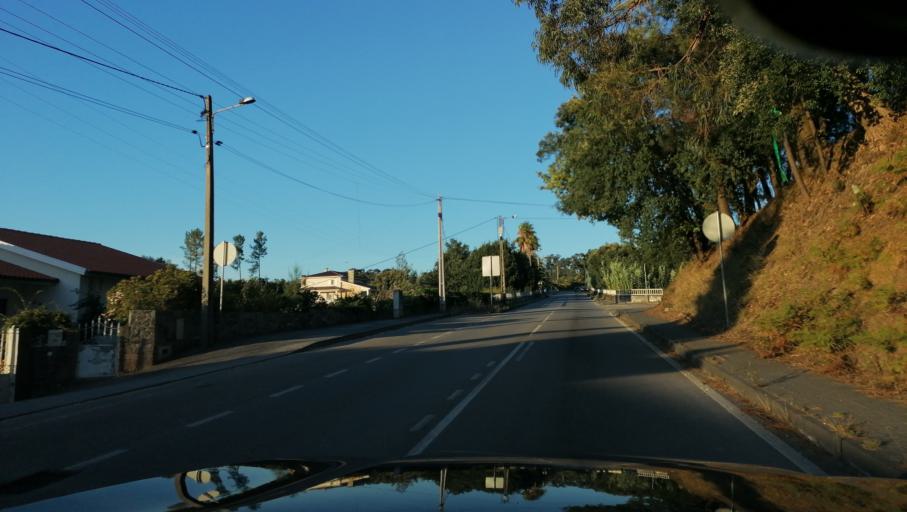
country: PT
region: Aveiro
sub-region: Oliveira do Bairro
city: Oliveira do Bairro
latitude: 40.5583
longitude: -8.4868
